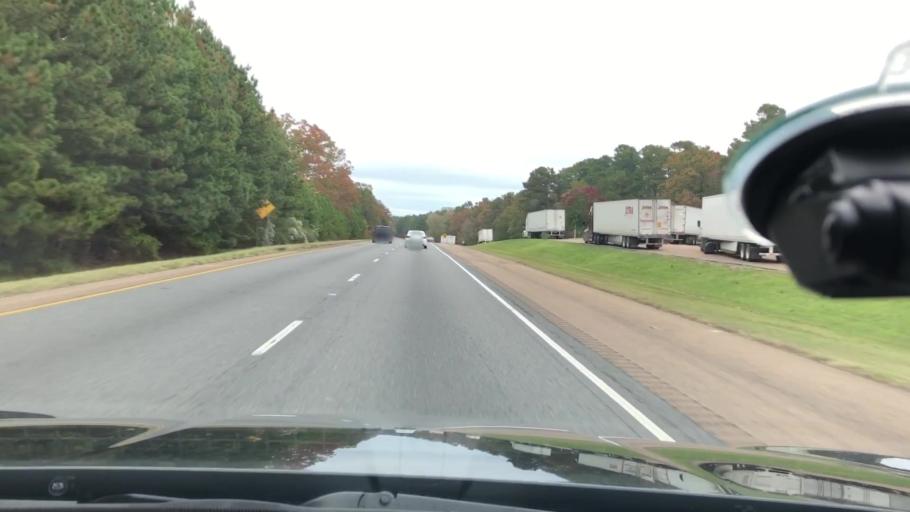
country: US
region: Arkansas
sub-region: Clark County
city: Gurdon
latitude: 33.9293
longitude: -93.2609
